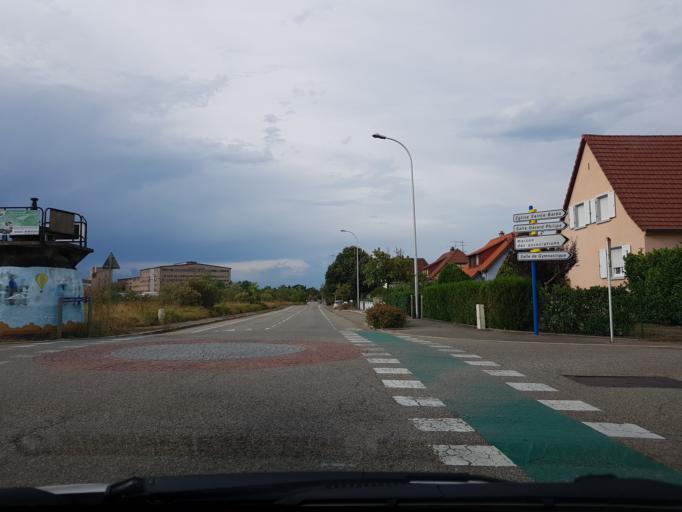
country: FR
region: Alsace
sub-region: Departement du Haut-Rhin
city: Wittenheim
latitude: 47.8234
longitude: 7.3312
